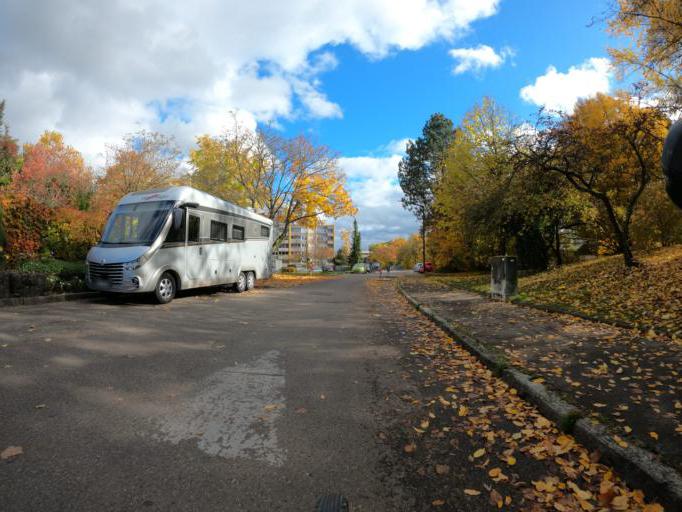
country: DE
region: Baden-Wuerttemberg
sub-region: Regierungsbezirk Stuttgart
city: Magstadt
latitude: 48.7196
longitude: 8.9621
